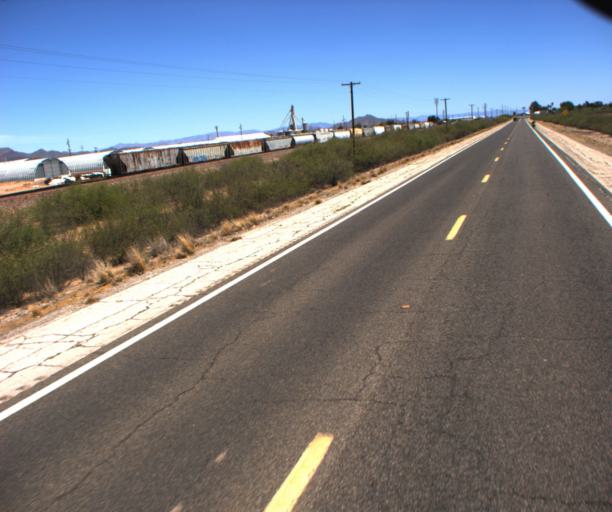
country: US
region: Arizona
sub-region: Yavapai County
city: Congress
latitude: 33.9405
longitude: -113.1864
